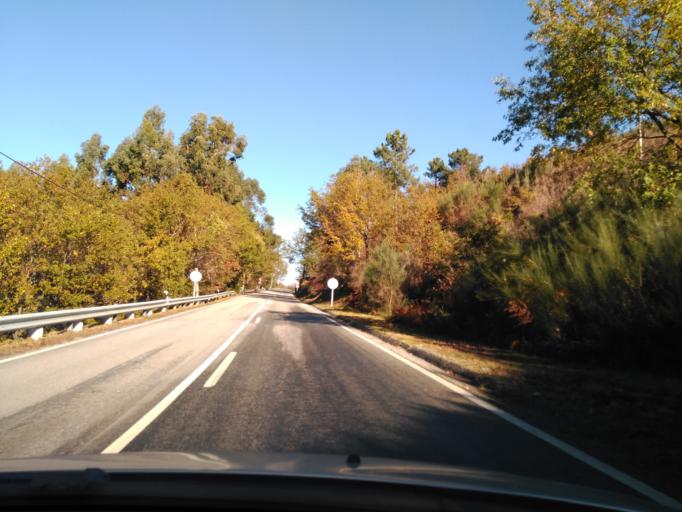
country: PT
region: Braga
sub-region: Vieira do Minho
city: Vieira do Minho
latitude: 41.6817
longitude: -8.0098
